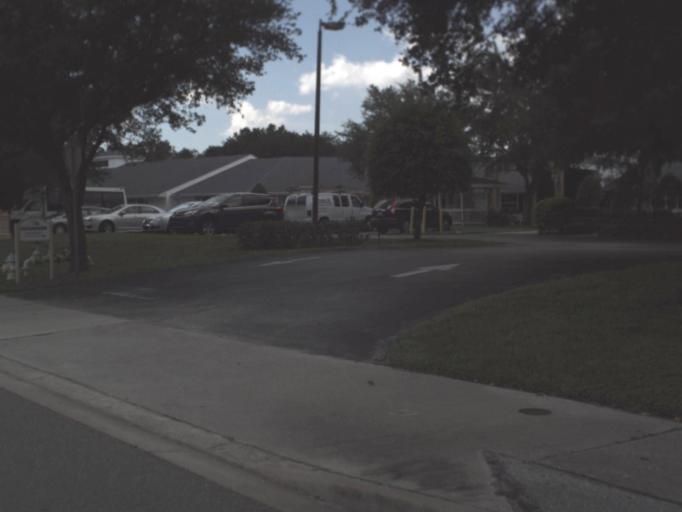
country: US
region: Florida
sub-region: Sarasota County
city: Kensington Park
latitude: 27.3376
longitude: -82.5044
